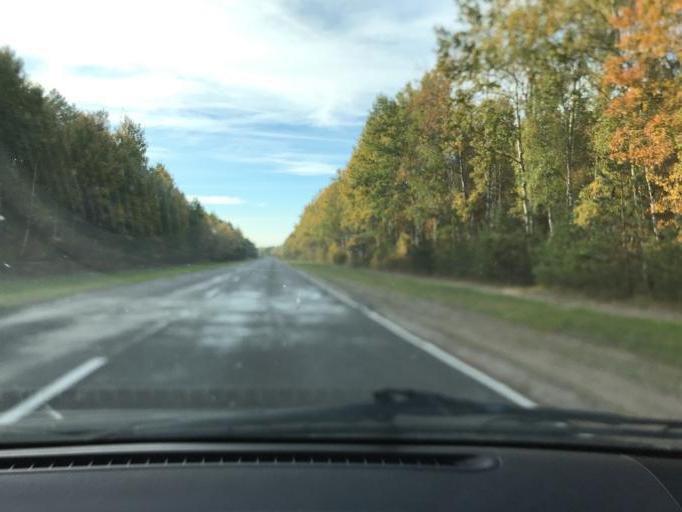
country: BY
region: Brest
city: Ivanava
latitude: 52.1564
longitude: 25.7722
